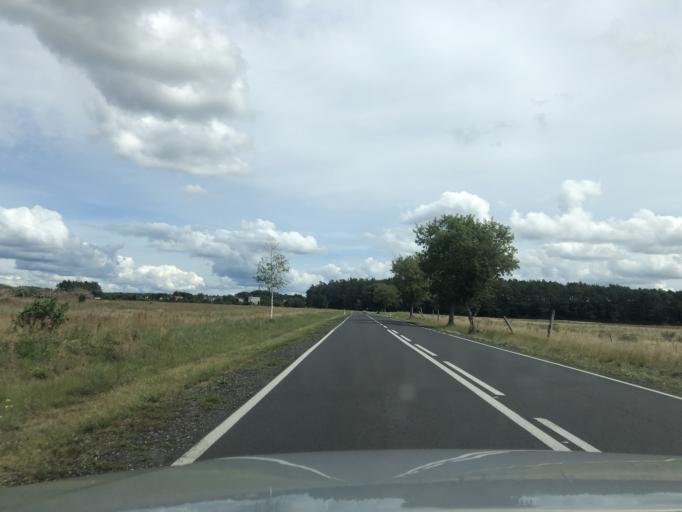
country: PL
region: Greater Poland Voivodeship
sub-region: Powiat pilski
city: Szydlowo
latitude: 53.0751
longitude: 16.5874
